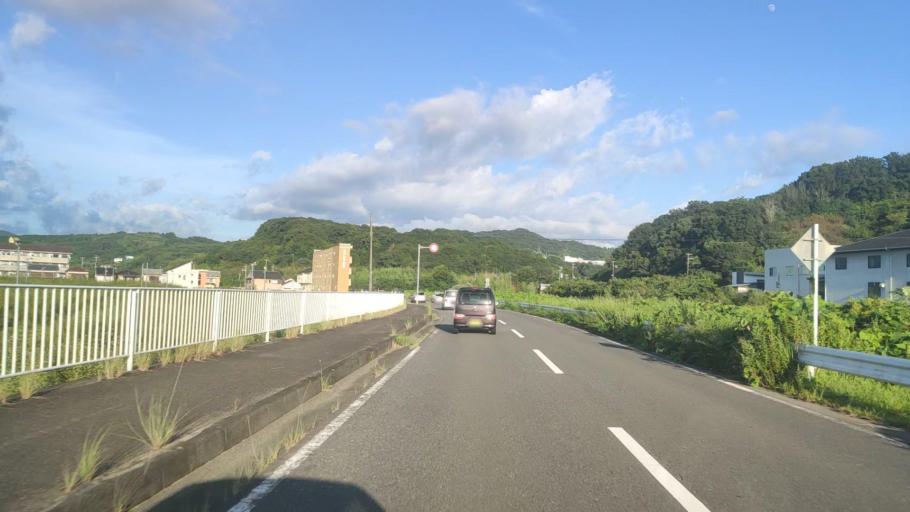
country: JP
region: Wakayama
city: Tanabe
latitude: 33.7334
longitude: 135.4157
